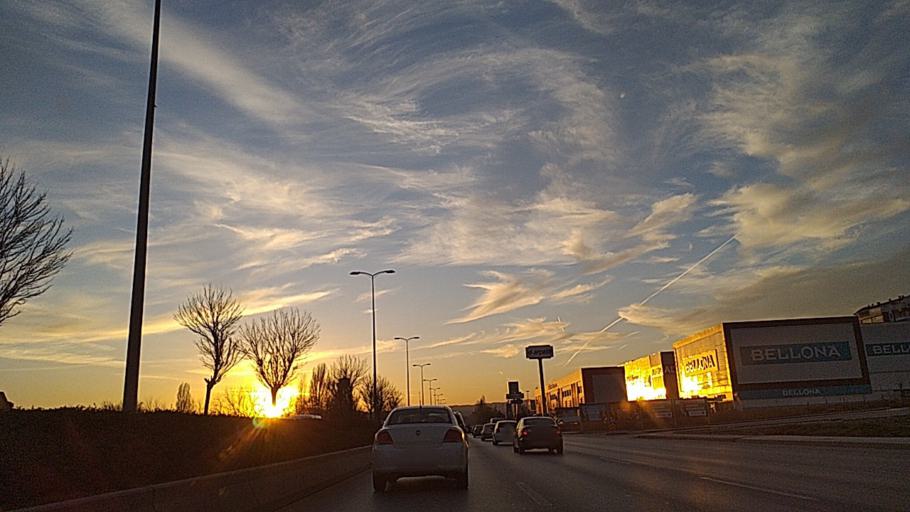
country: TR
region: Ankara
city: Etimesgut
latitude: 39.9630
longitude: 32.6559
